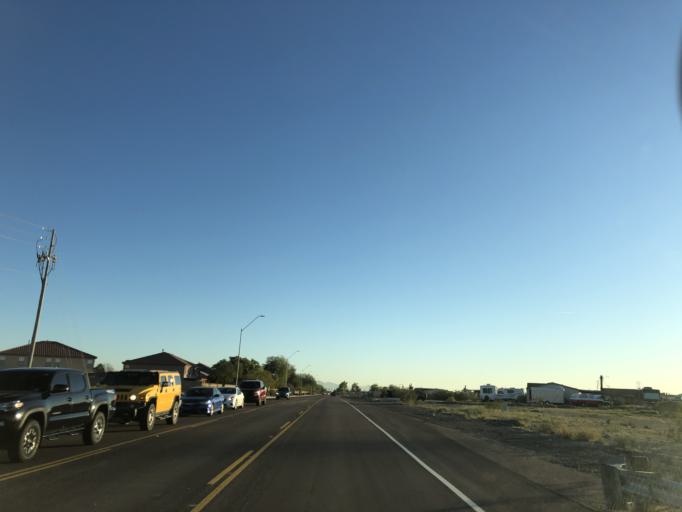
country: US
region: Arizona
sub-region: Maricopa County
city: Sun City West
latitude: 33.6954
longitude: -112.2897
